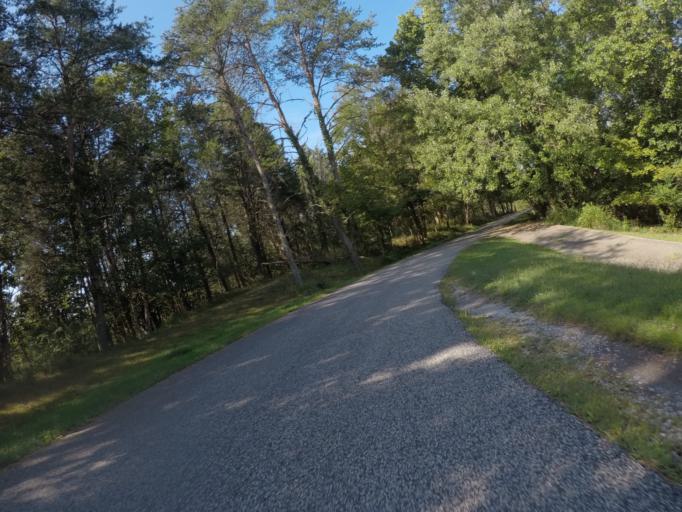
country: US
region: West Virginia
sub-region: Cabell County
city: Barboursville
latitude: 38.3640
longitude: -82.2738
